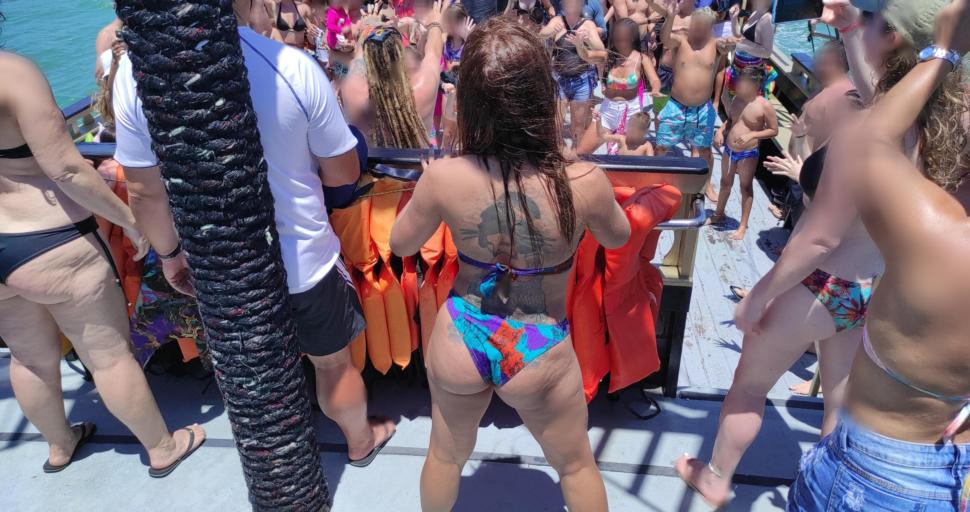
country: BR
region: Santa Catarina
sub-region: Porto Belo
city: Porto Belo
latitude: -27.1996
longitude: -48.5201
